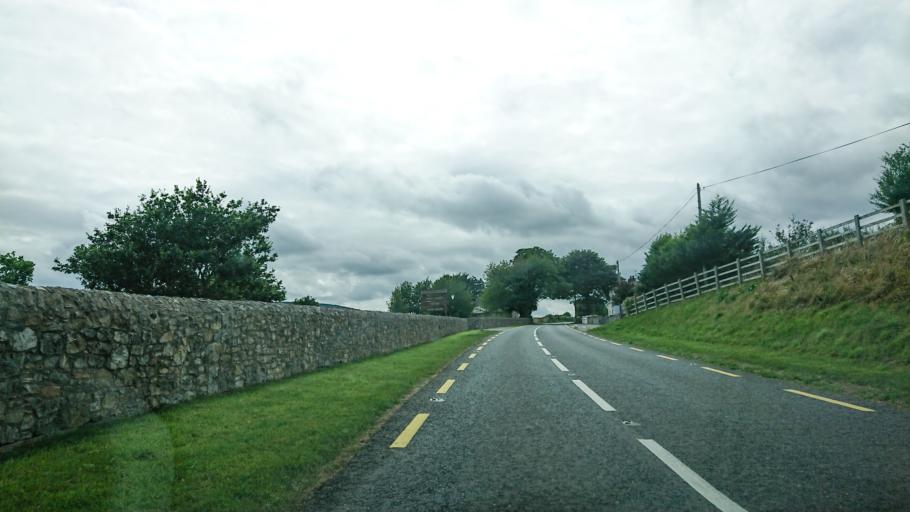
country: IE
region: Munster
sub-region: County Cork
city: Mallow
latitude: 52.1535
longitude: -8.5233
